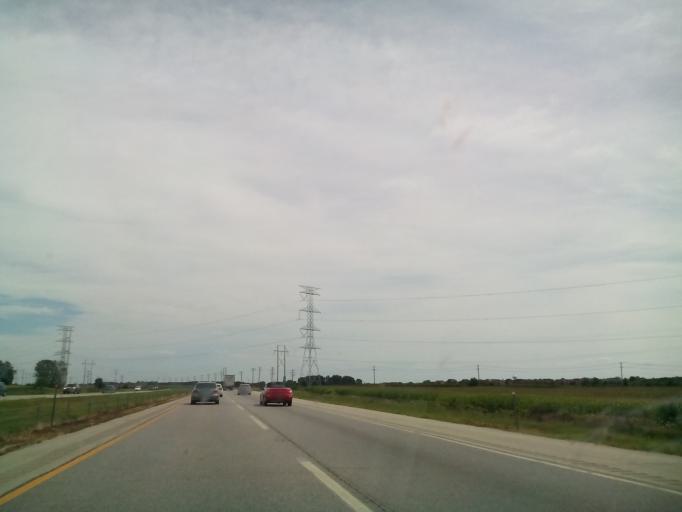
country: US
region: Illinois
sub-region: Kane County
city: Sugar Grove
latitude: 41.8074
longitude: -88.4394
